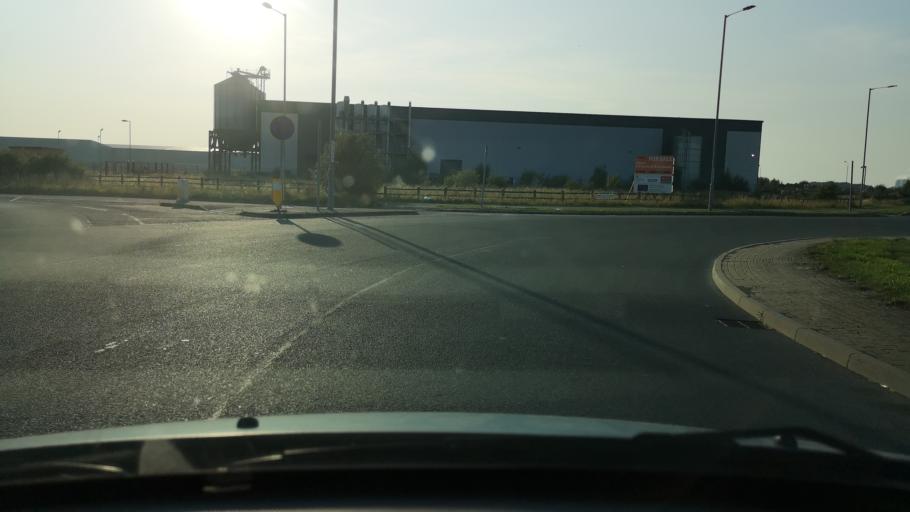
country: GB
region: England
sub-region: East Riding of Yorkshire
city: Airmyn
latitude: 53.7001
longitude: -0.9054
